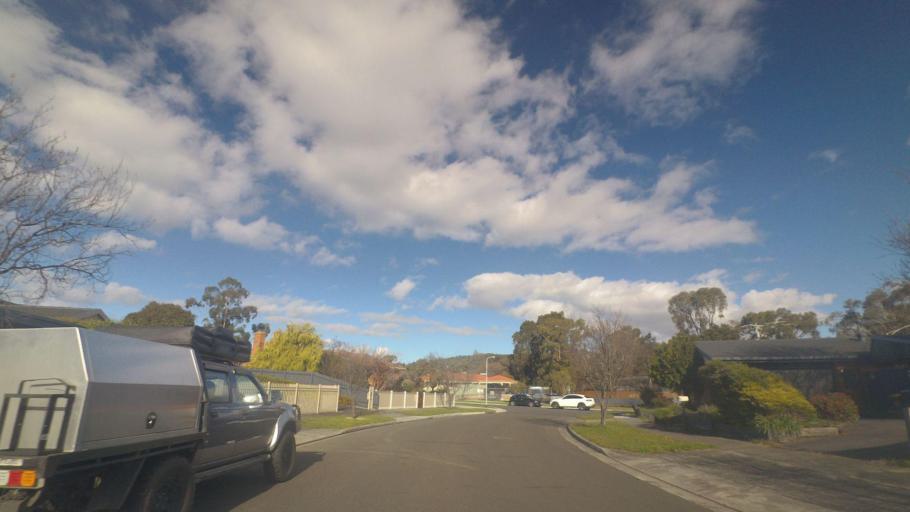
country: AU
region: Victoria
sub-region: Yarra Ranges
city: Lysterfield
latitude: -37.9153
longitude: 145.2756
